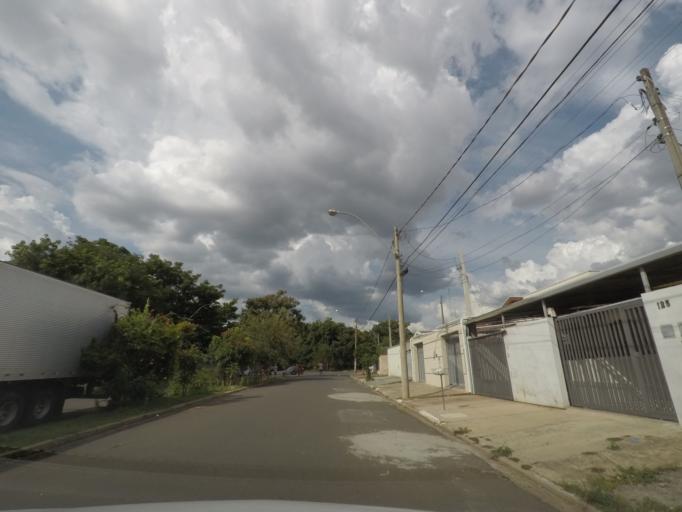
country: BR
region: Sao Paulo
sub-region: Campinas
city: Campinas
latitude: -22.8851
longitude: -47.1085
